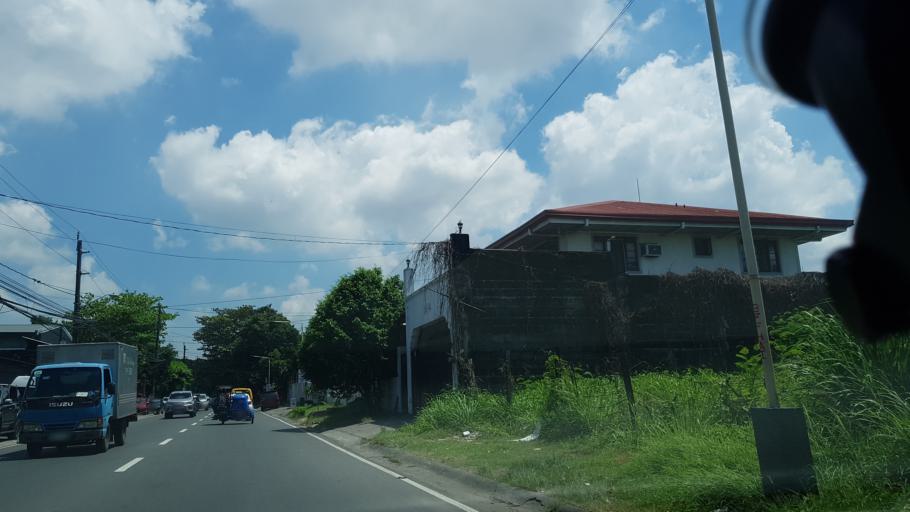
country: PH
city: Sambayanihan People's Village
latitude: 14.4487
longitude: 121.0080
